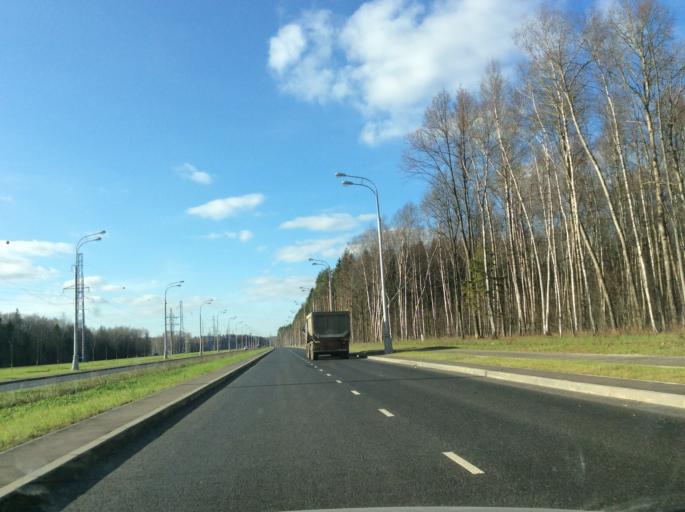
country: RU
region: Moskovskaya
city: Vatutinki
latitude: 55.4833
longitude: 37.3536
